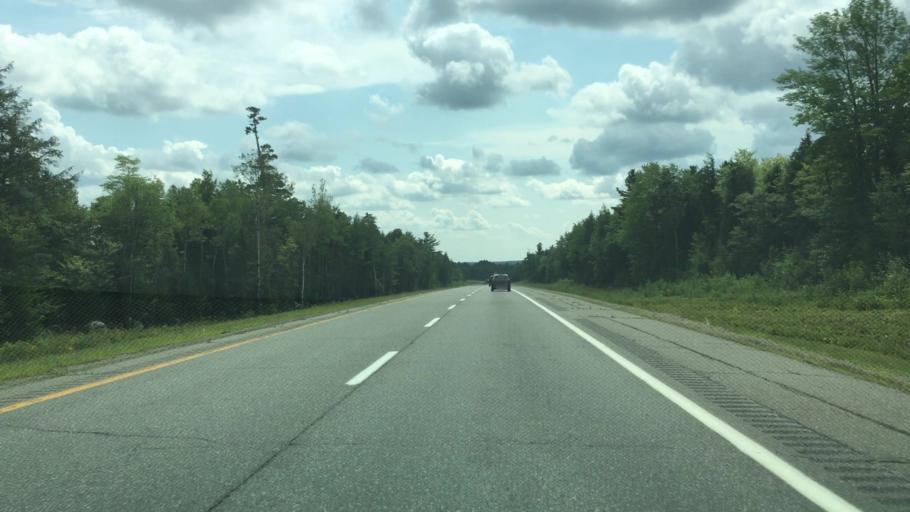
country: US
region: Maine
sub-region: Penobscot County
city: Howland
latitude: 45.2808
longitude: -68.6719
